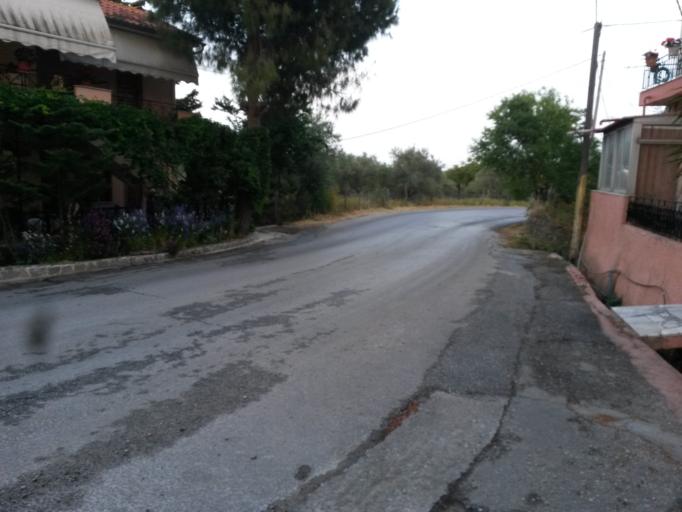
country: GR
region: North Aegean
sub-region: Nomos Lesvou
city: Pamfylla
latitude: 39.1770
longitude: 26.5003
